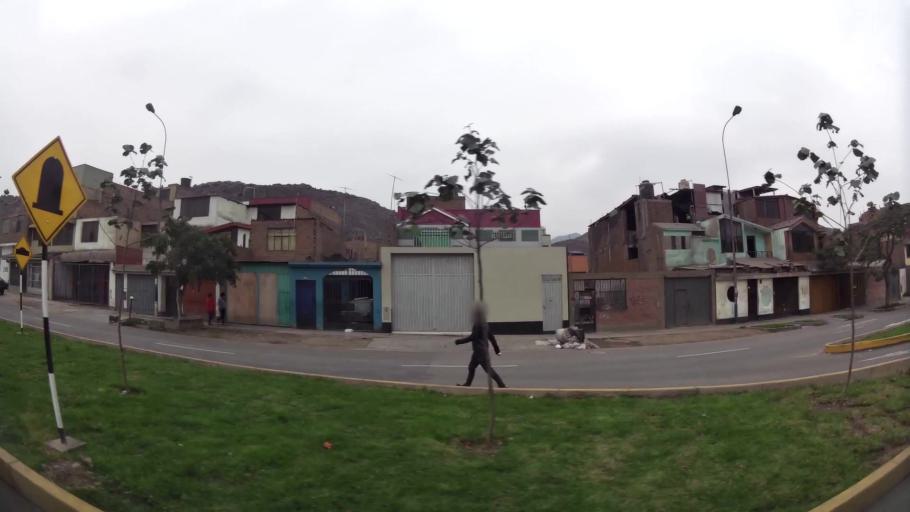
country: PE
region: Lima
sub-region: Lima
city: Vitarte
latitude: -12.0448
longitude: -76.9345
